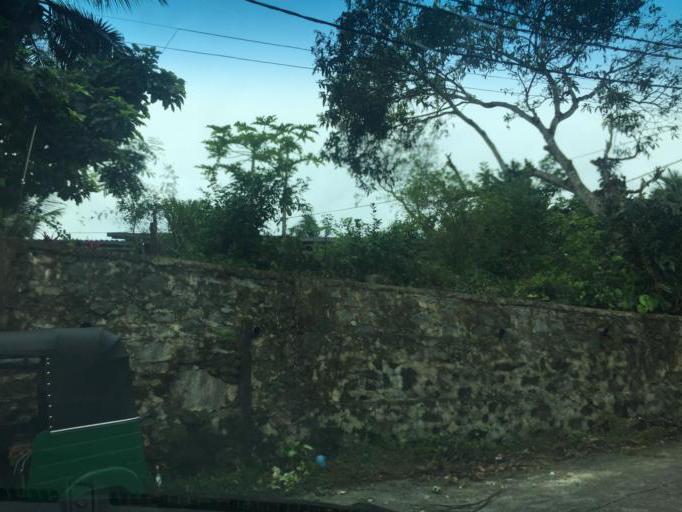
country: LK
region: Western
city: Horana South
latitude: 6.7134
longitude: 80.0612
